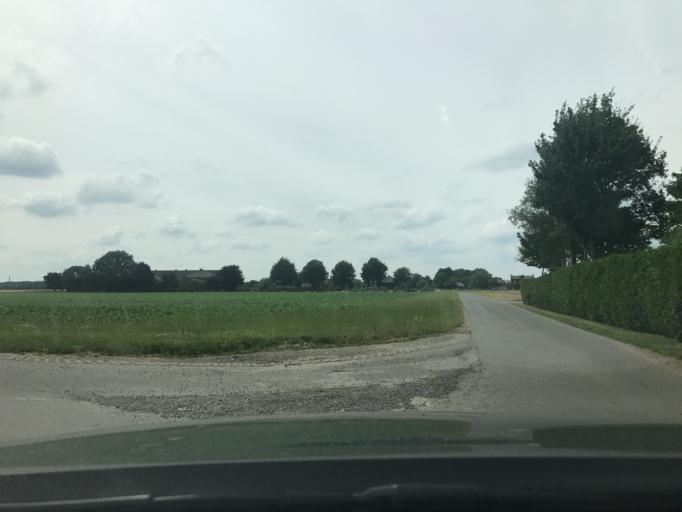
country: DE
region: North Rhine-Westphalia
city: Kempen
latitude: 51.3395
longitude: 6.4187
